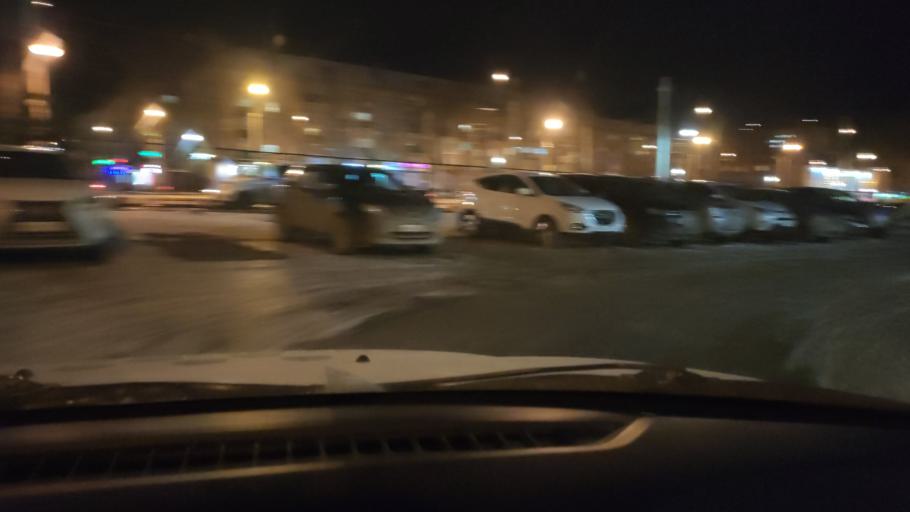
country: RU
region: Perm
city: Perm
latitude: 57.9977
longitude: 56.2863
